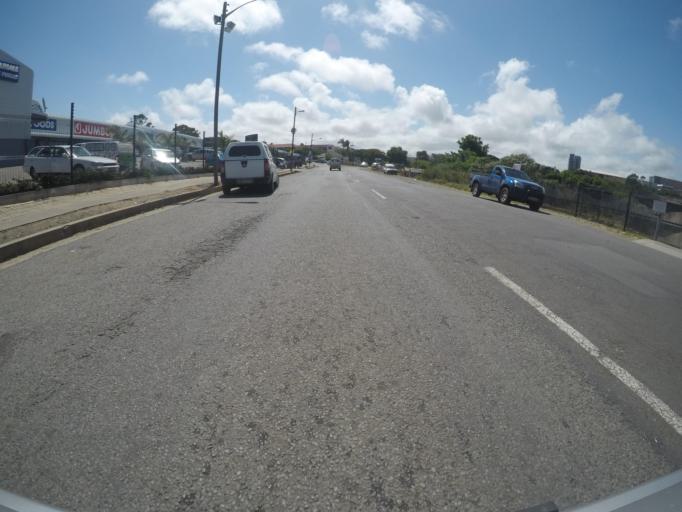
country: ZA
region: Eastern Cape
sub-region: Buffalo City Metropolitan Municipality
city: East London
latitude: -33.0052
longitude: 27.9081
